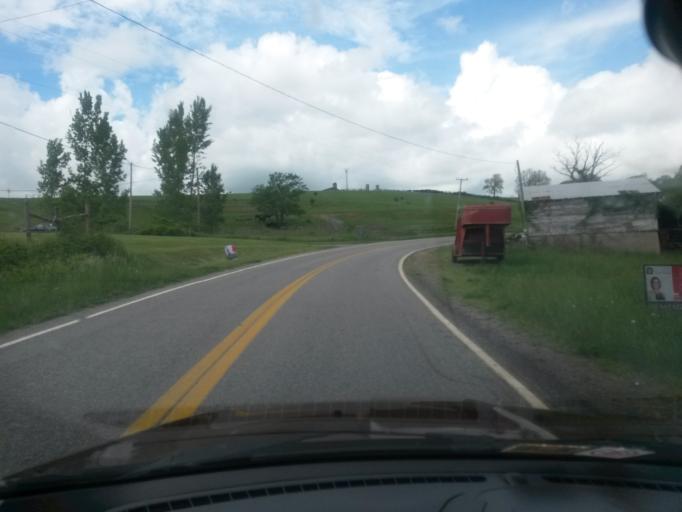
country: US
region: Virginia
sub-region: Floyd County
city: Floyd
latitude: 36.7657
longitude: -80.3915
